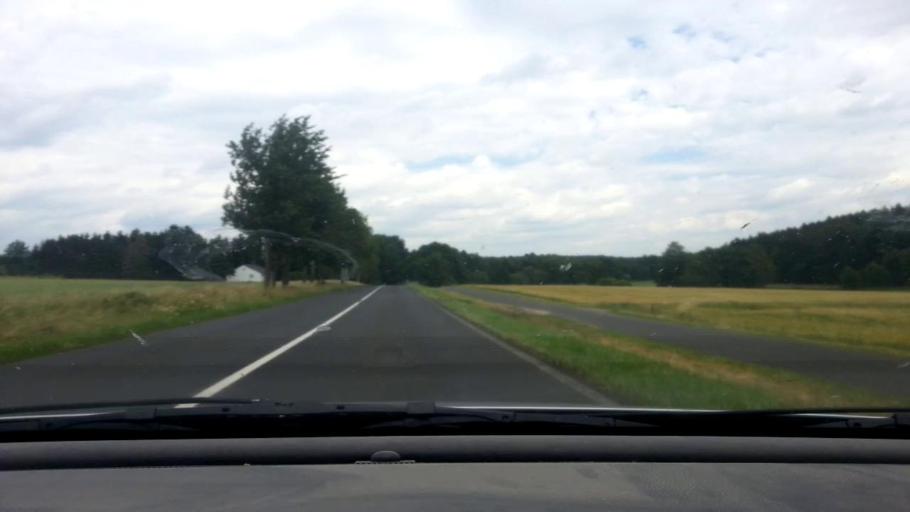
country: DE
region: Bavaria
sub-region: Upper Palatinate
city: Waldsassen
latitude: 50.0187
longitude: 12.3213
